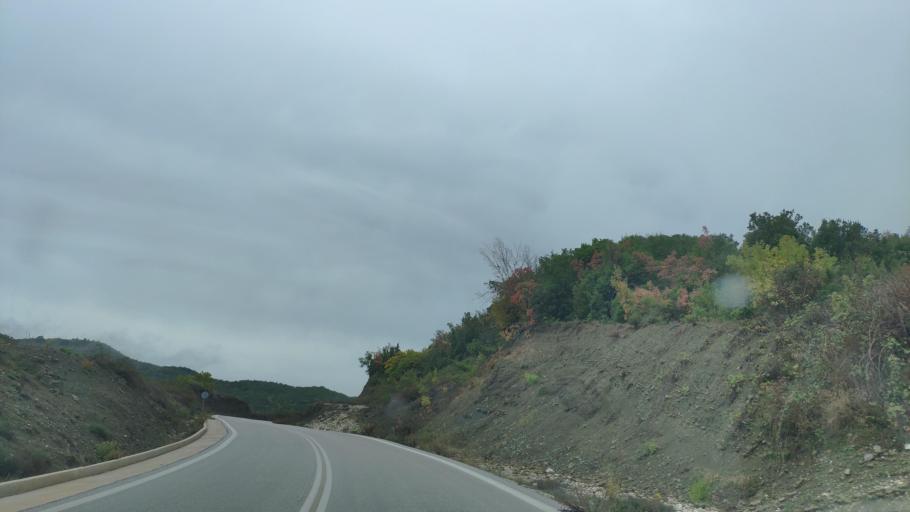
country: GR
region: Epirus
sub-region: Nomos Thesprotias
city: Paramythia
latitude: 39.4852
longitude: 20.6720
